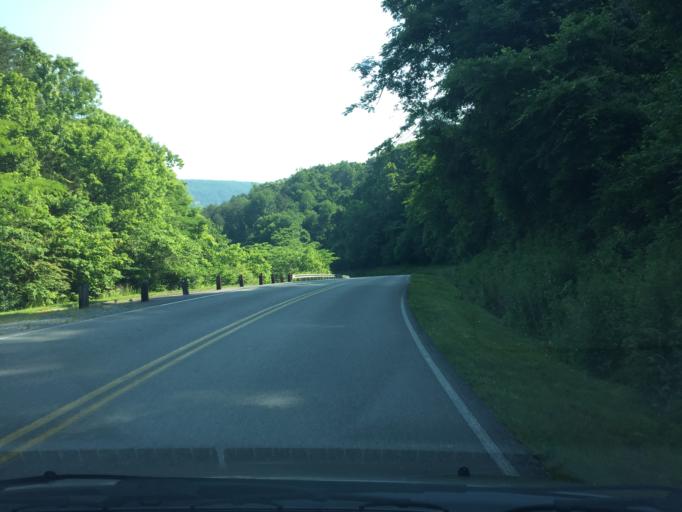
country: US
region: Tennessee
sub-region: Hamilton County
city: Lookout Mountain
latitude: 35.0504
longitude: -85.4250
